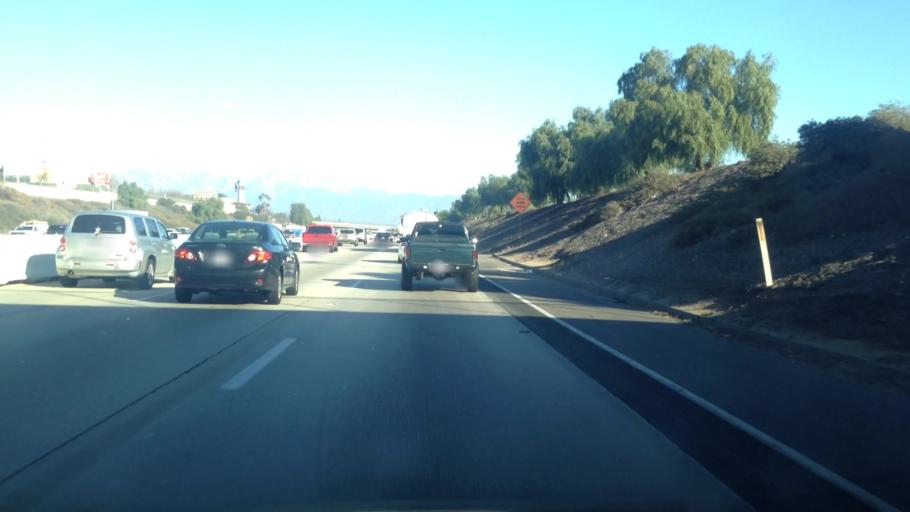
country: US
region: California
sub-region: Riverside County
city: Norco
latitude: 33.9312
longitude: -117.5559
